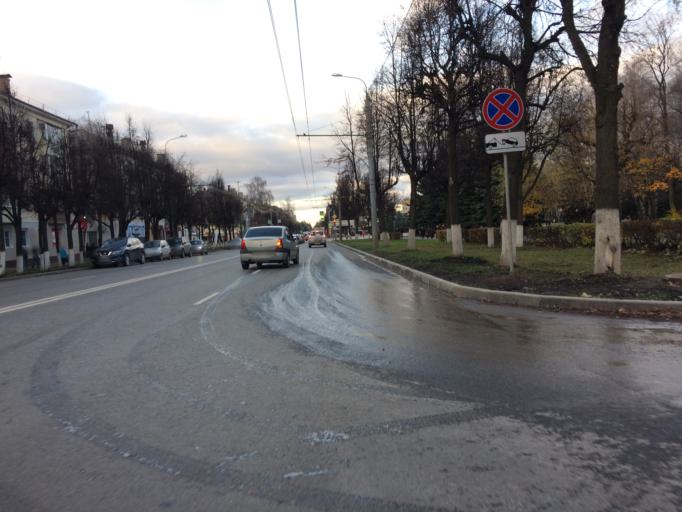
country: RU
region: Mariy-El
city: Yoshkar-Ola
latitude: 56.6361
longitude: 47.8858
